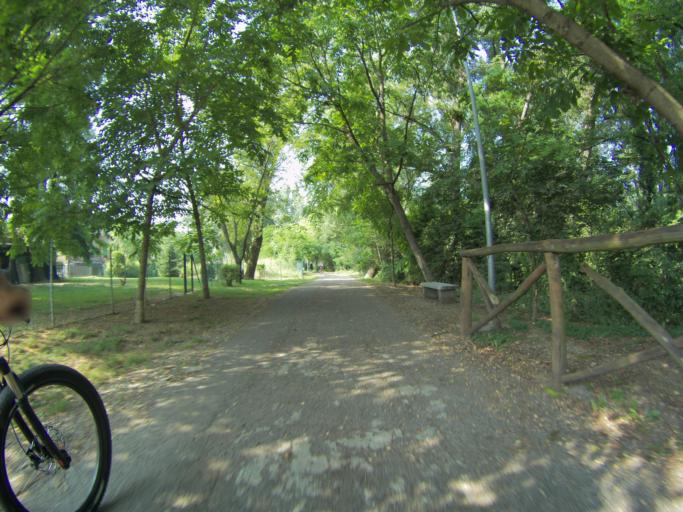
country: IT
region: Emilia-Romagna
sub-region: Provincia di Reggio Emilia
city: Ventoso
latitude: 44.5891
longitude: 10.6734
